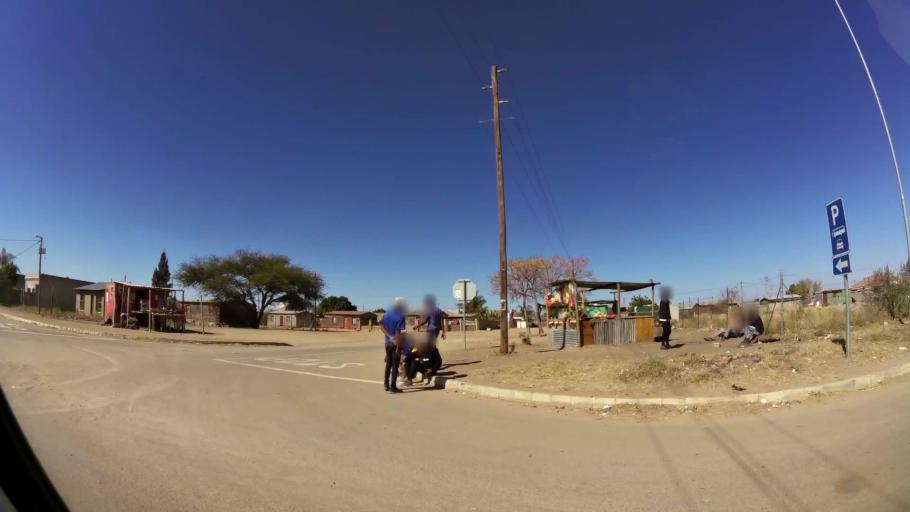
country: ZA
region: Limpopo
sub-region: Capricorn District Municipality
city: Polokwane
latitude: -23.8500
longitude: 29.4144
